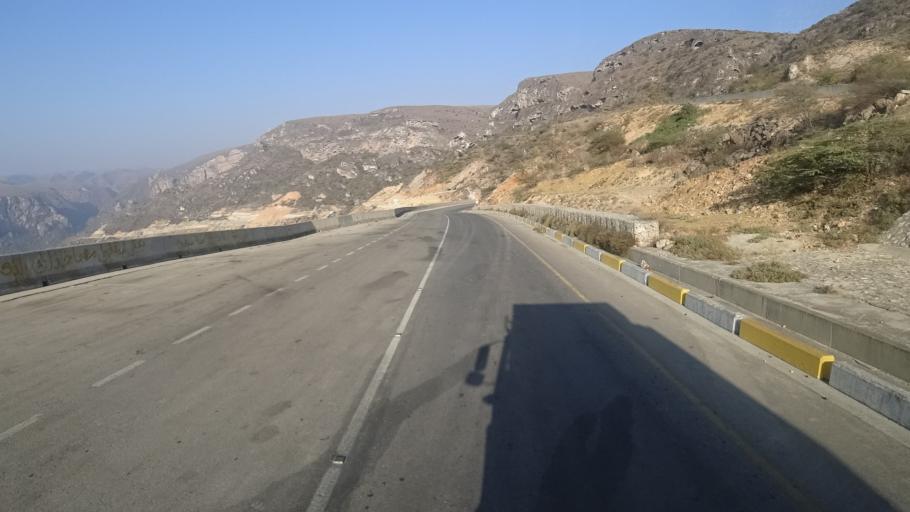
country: YE
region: Al Mahrah
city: Hawf
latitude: 16.7551
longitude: 53.2325
